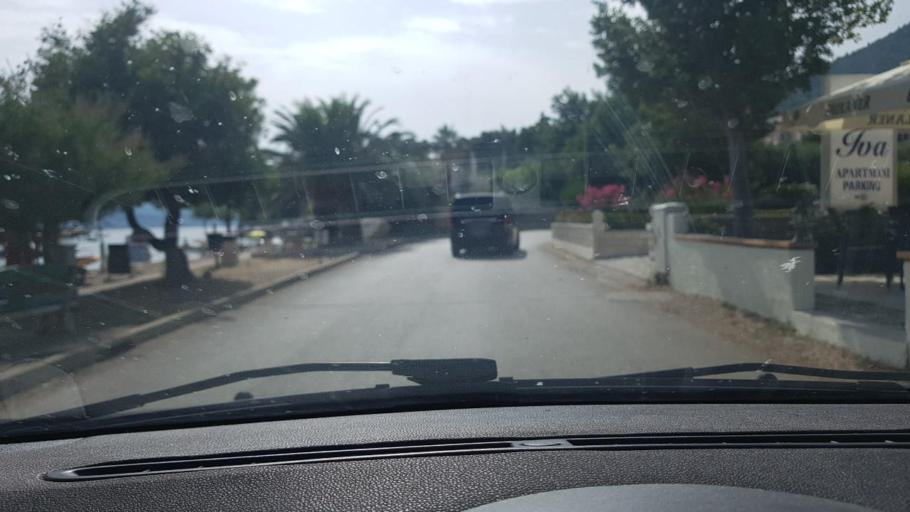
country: HR
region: Dubrovacko-Neretvanska
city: Orebic
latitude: 42.9749
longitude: 17.1693
